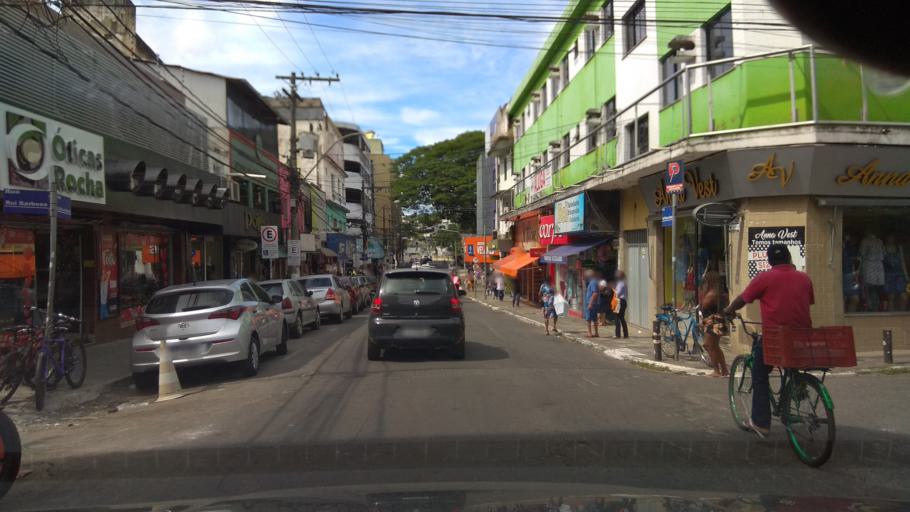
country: BR
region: Bahia
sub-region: Itabuna
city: Itabuna
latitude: -14.7918
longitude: -39.2760
